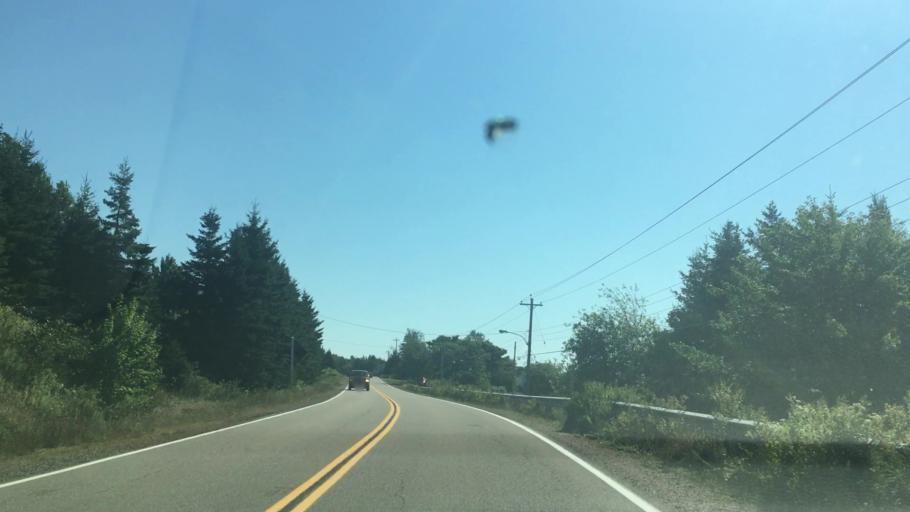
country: CA
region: Nova Scotia
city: Antigonish
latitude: 45.0267
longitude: -62.0285
